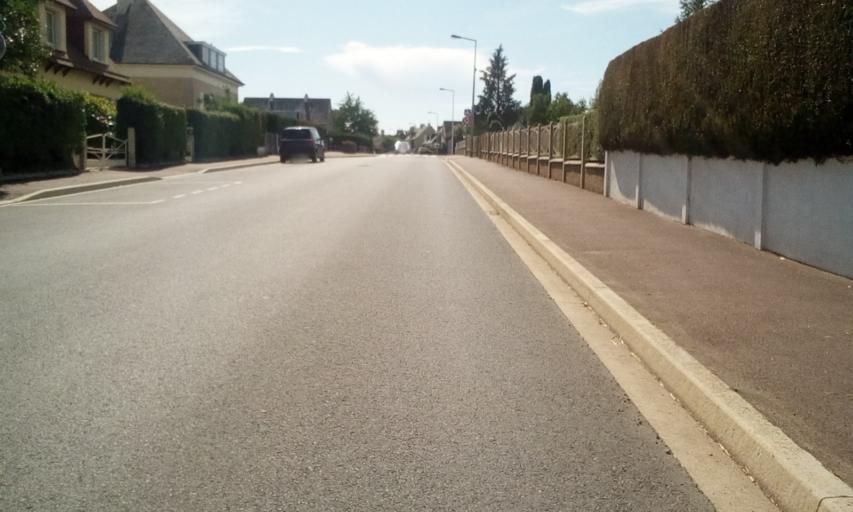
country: FR
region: Lower Normandy
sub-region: Departement du Calvados
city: Eterville
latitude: 49.1310
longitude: -0.4192
